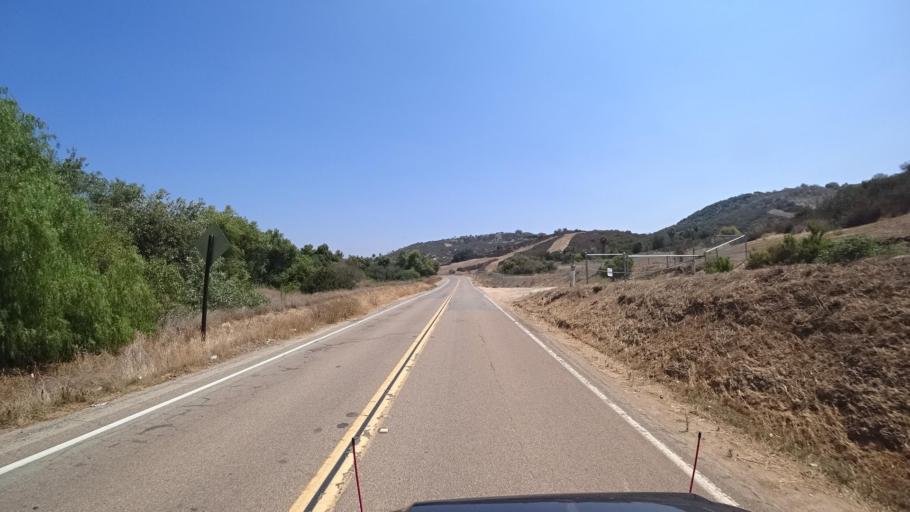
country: US
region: California
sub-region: San Diego County
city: Bonsall
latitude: 33.2767
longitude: -117.2249
